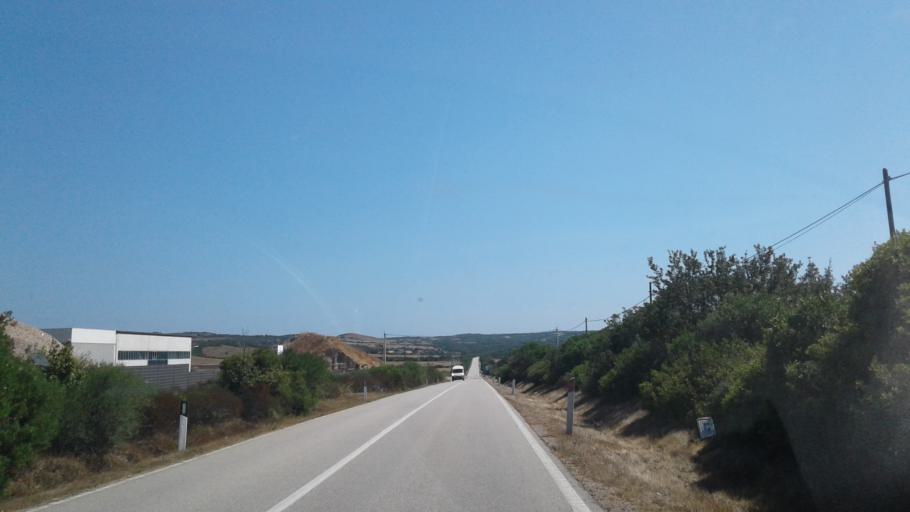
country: IT
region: Sardinia
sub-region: Provincia di Olbia-Tempio
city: Luogosanto
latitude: 41.1168
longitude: 9.2659
